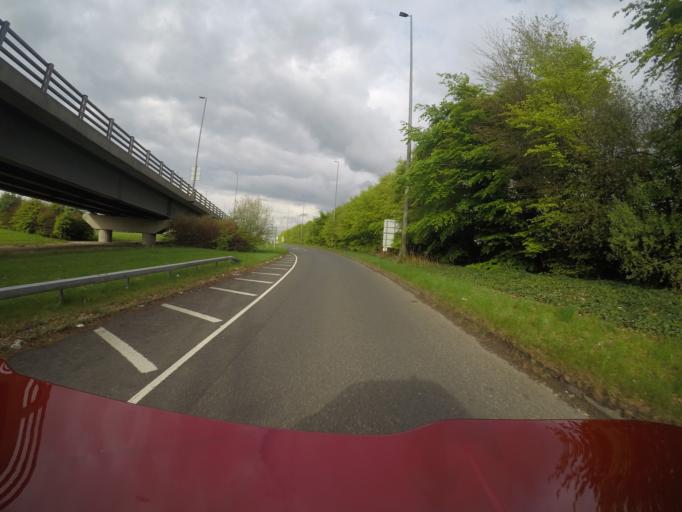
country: GB
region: Scotland
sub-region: Renfrewshire
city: Paisley
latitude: 55.8586
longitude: -4.4444
